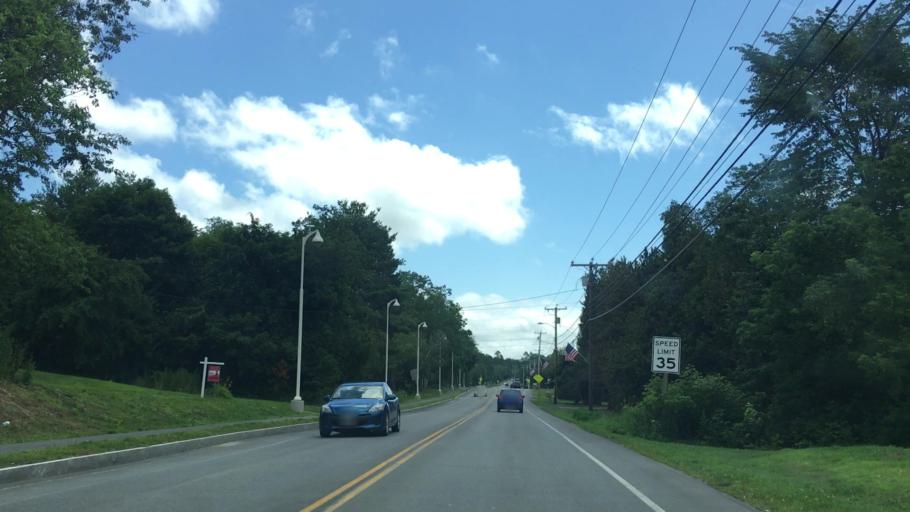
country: US
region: Maine
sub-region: Penobscot County
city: Hermon
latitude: 44.8075
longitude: -68.9060
